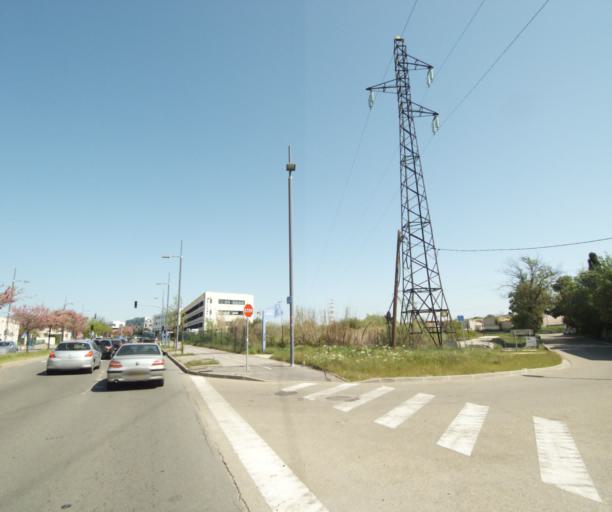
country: FR
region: Languedoc-Roussillon
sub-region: Departement de l'Herault
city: Castelnau-le-Lez
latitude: 43.6136
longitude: 3.9148
